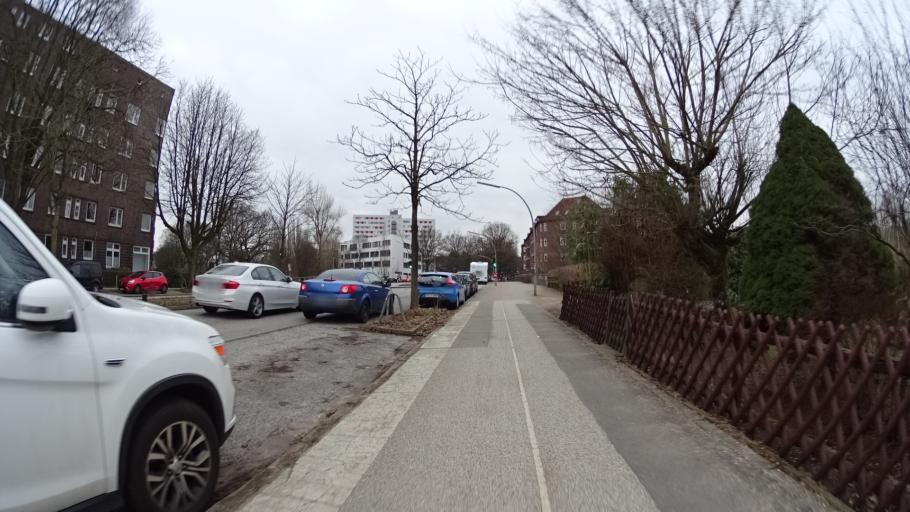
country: DE
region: Hamburg
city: Hamburg
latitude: 53.5893
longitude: 10.0215
